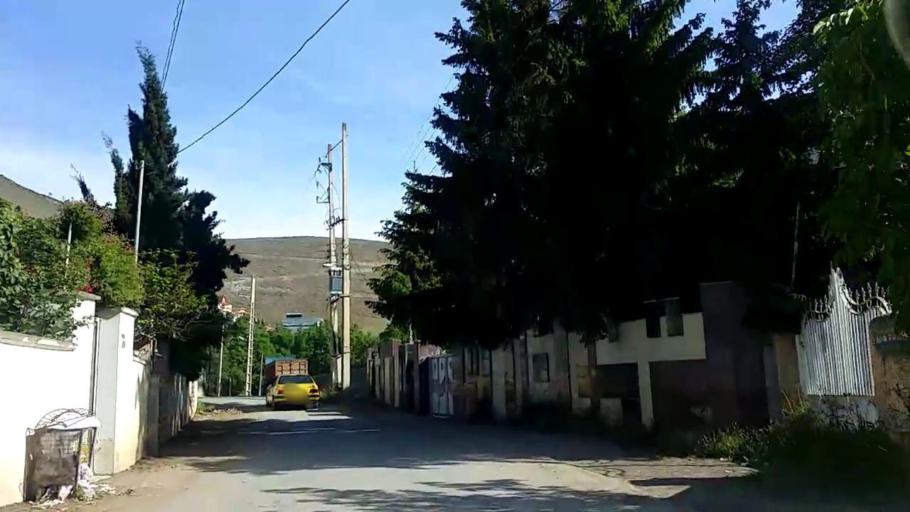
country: IR
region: Mazandaran
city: `Abbasabad
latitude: 36.5032
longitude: 51.1573
